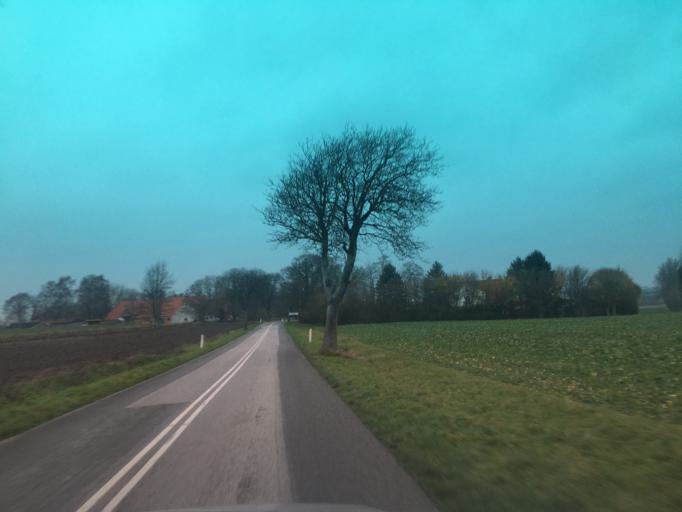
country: DK
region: Zealand
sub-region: Slagelse Kommune
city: Skaelskor
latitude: 55.2630
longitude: 11.4163
